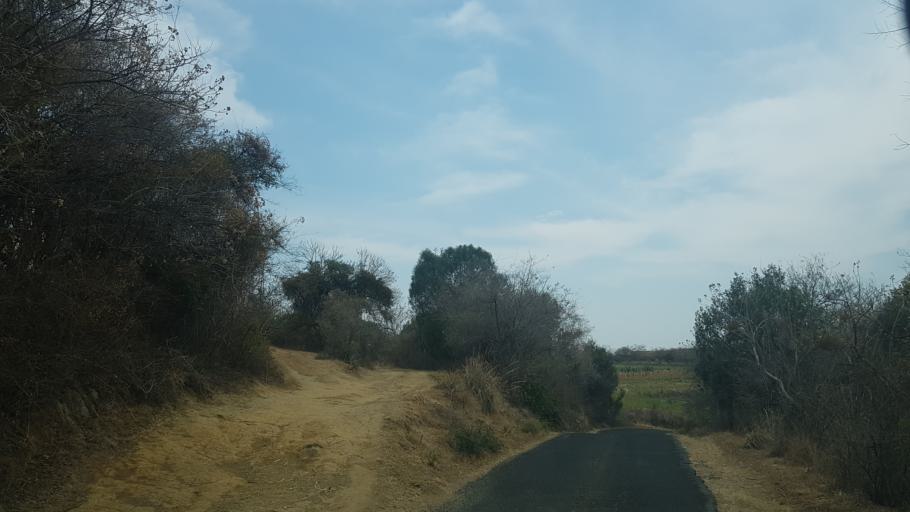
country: MX
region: Puebla
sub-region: Atzitzihuacan
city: Santiago Atzitzihuacan
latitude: 18.8413
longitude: -98.6123
